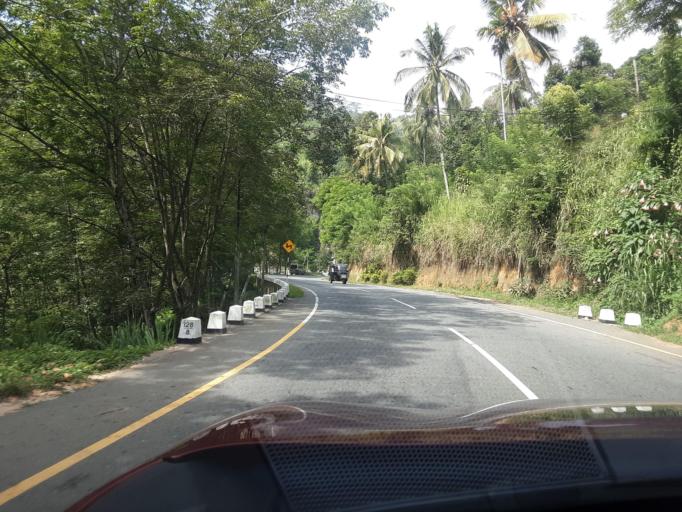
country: LK
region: Uva
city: Badulla
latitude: 6.9668
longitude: 81.0903
